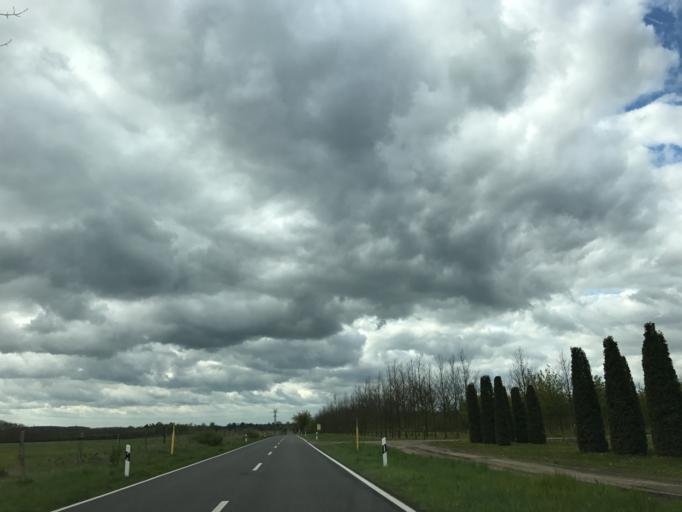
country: DE
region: Brandenburg
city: Pawesin
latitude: 52.5585
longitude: 12.7678
